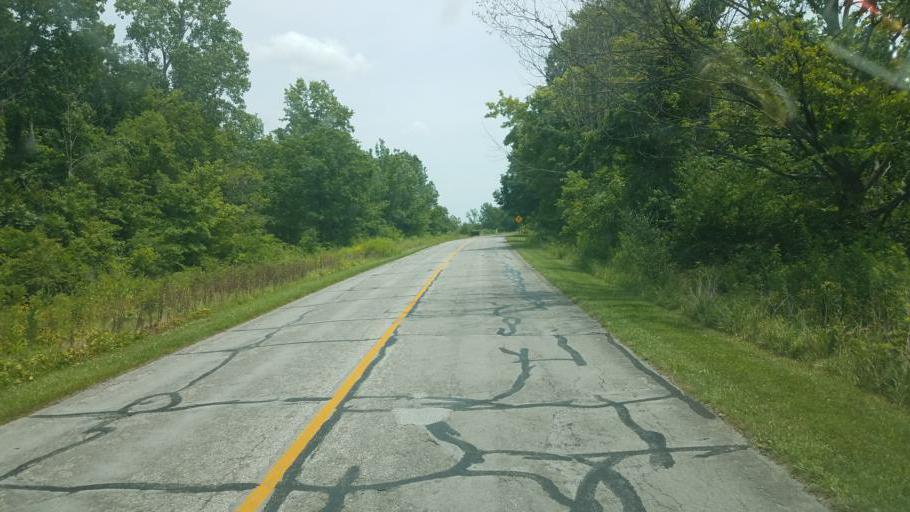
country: US
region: Ohio
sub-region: Delaware County
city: Powell
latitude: 40.1511
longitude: -83.0274
